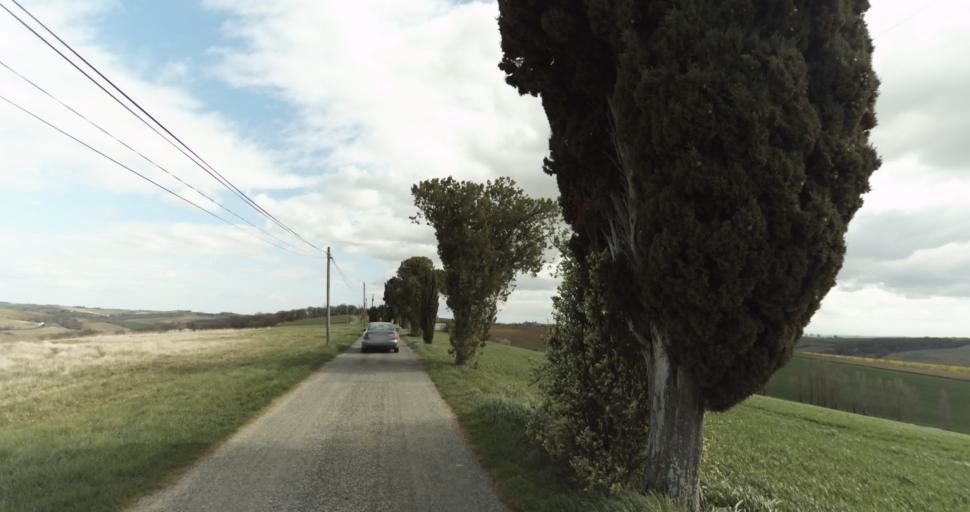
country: FR
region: Midi-Pyrenees
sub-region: Departement de la Haute-Garonne
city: Auterive
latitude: 43.3807
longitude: 1.4929
